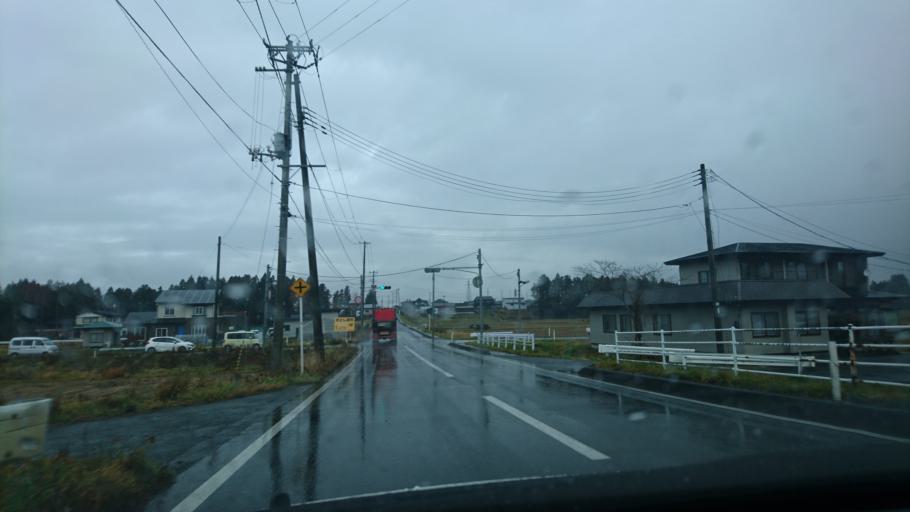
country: JP
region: Iwate
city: Kitakami
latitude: 39.2923
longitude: 141.0550
